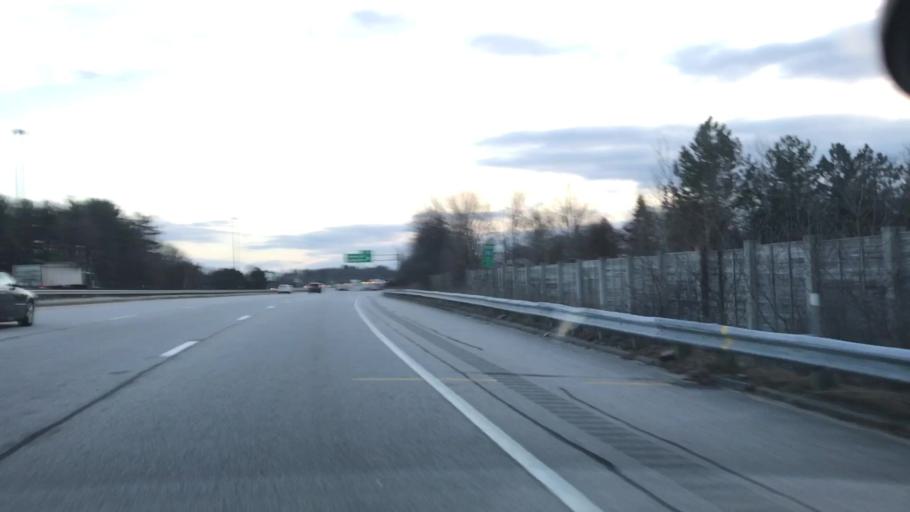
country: US
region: New Hampshire
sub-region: Hillsborough County
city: Manchester
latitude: 42.9931
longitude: -71.4176
